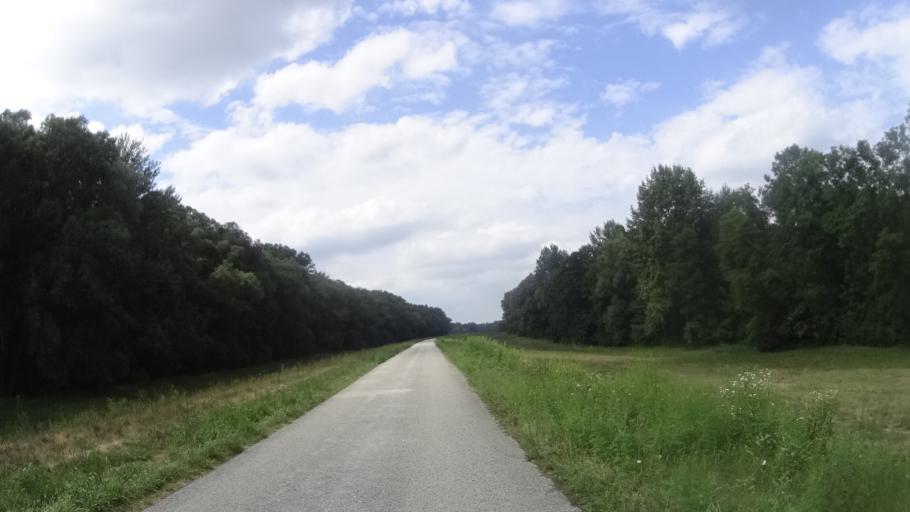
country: SK
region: Trnavsky
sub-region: Okres Dunajska Streda
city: Velky Meder
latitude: 47.7763
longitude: 17.7078
